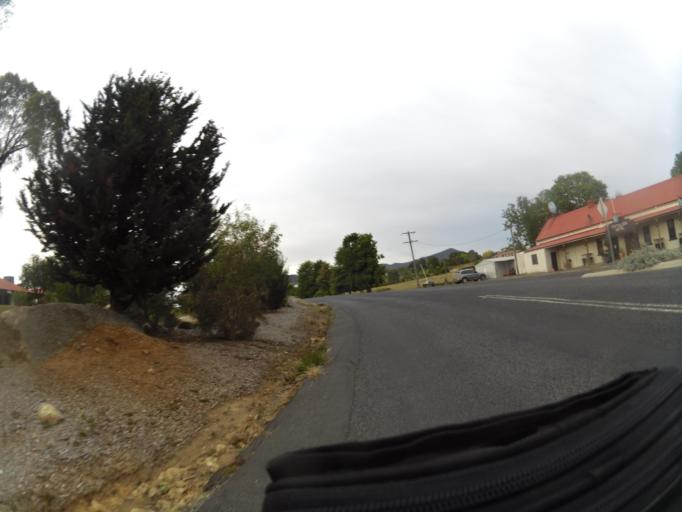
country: AU
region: New South Wales
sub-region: Greater Hume Shire
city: Holbrook
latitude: -36.0465
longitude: 147.9313
